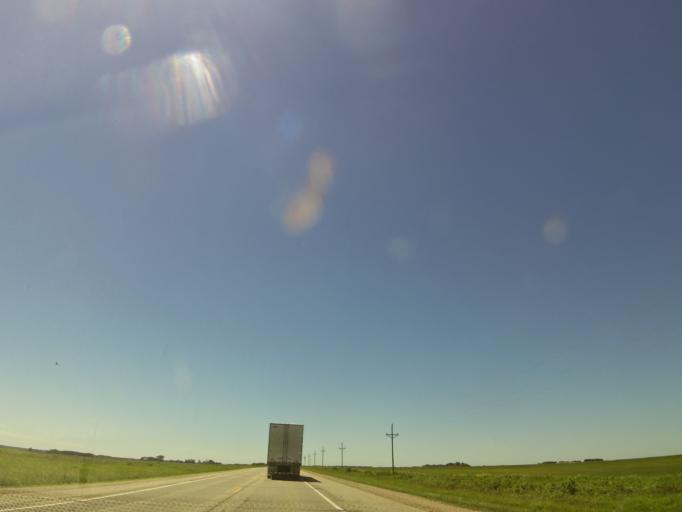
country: US
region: Minnesota
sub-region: Mahnomen County
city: Mahnomen
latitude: 47.2429
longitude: -95.9335
